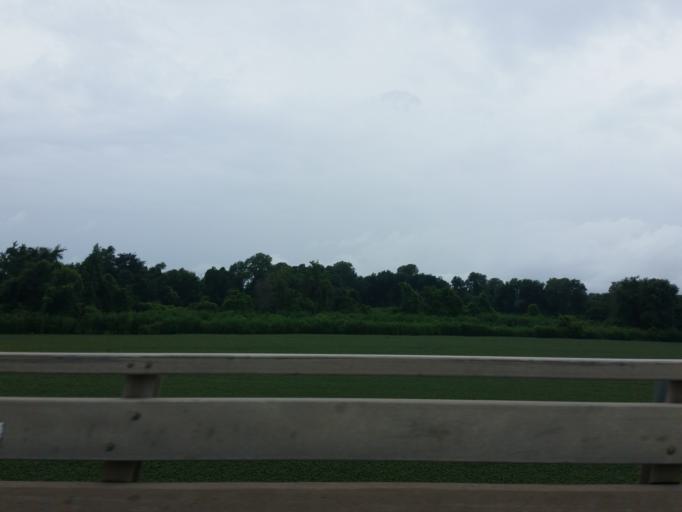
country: US
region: Illinois
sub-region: Alexander County
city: Cairo
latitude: 36.9740
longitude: -89.1461
